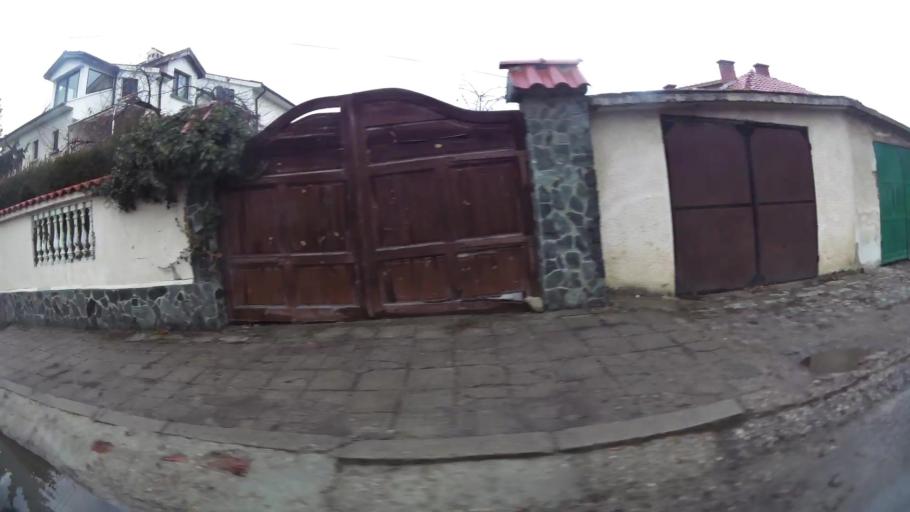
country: BG
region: Sofia-Capital
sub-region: Stolichna Obshtina
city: Sofia
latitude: 42.7355
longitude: 23.3404
